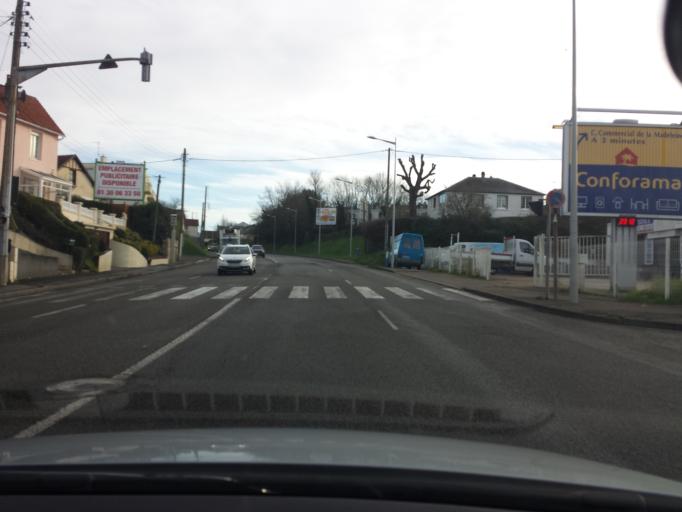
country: FR
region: Haute-Normandie
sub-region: Departement de l'Eure
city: Evreux
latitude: 49.0164
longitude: 1.1616
